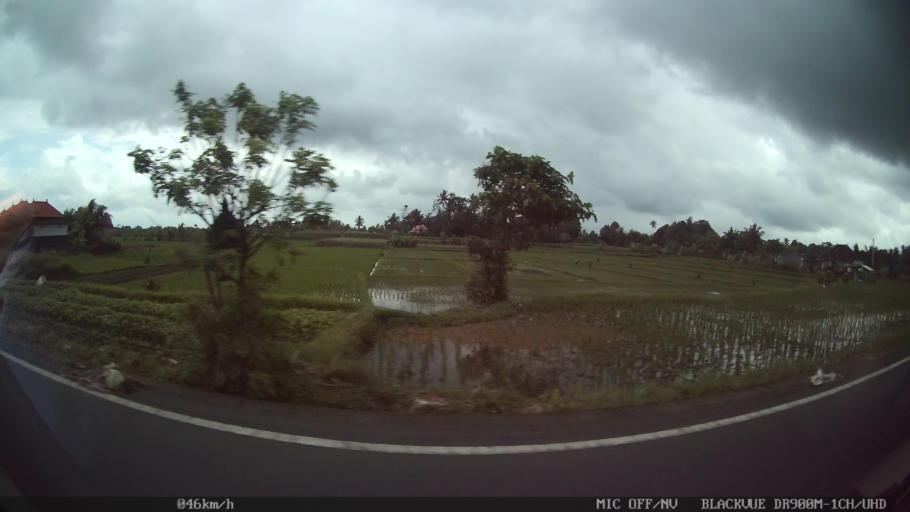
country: ID
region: Bali
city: Banjar Mambalkajanan
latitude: -8.5383
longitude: 115.2236
